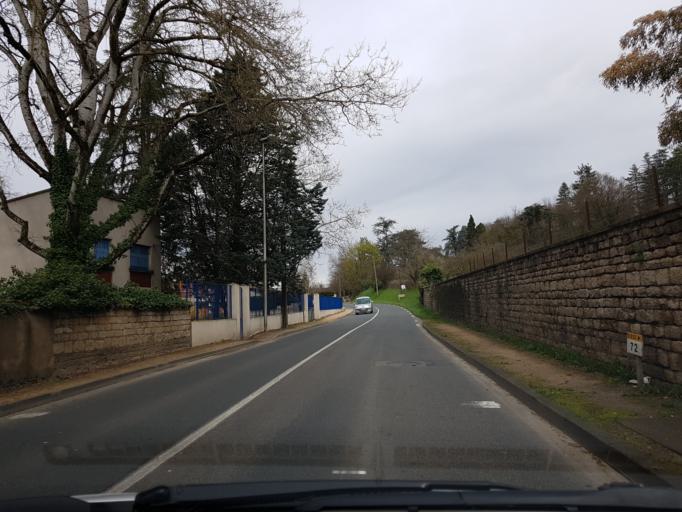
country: FR
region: Rhone-Alpes
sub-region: Departement de l'Ain
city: Trevoux
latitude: 45.9457
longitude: 4.7598
